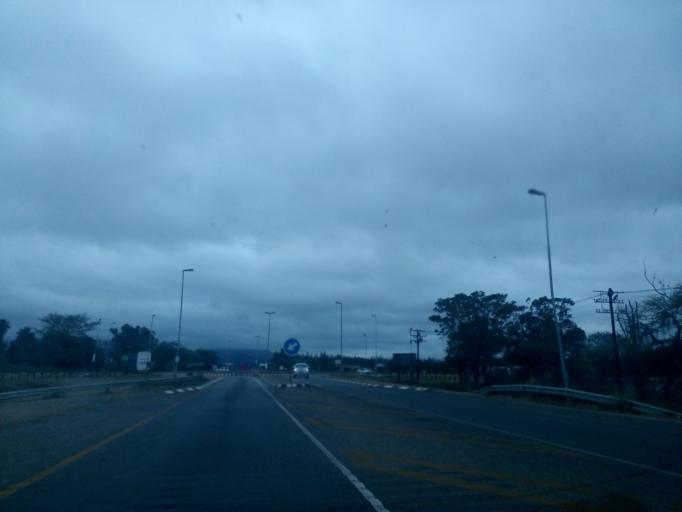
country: ZA
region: Limpopo
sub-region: Vhembe District Municipality
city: Louis Trichardt
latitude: -23.0794
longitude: 29.9083
